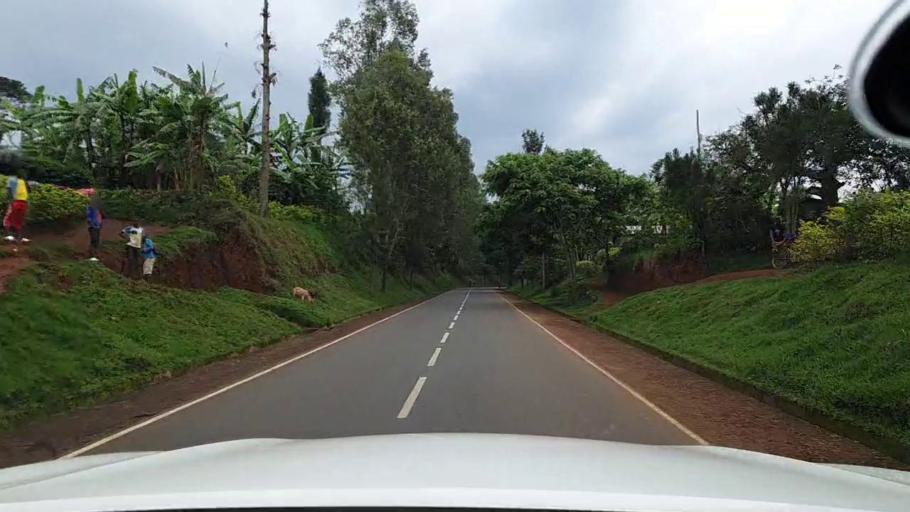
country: RW
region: Western Province
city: Cyangugu
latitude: -2.5386
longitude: 28.8980
